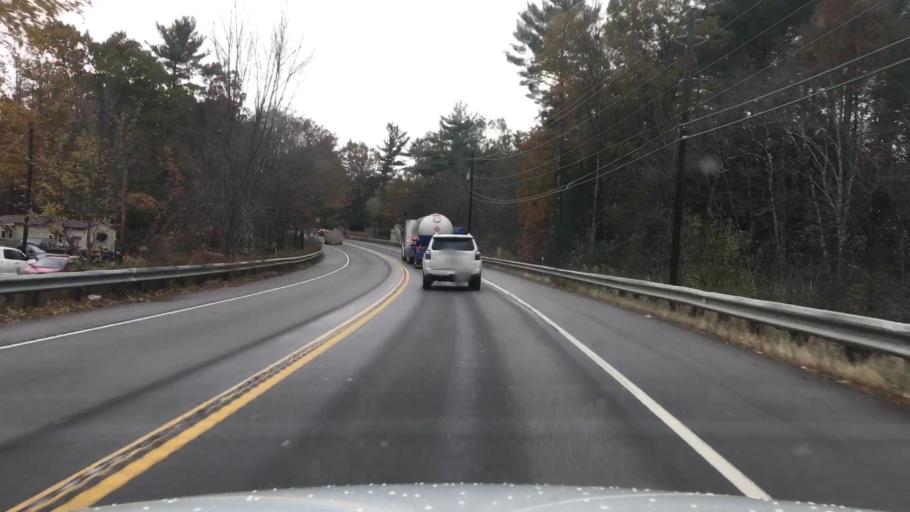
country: US
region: New Hampshire
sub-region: Strafford County
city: Lee
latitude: 43.1351
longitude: -71.0198
